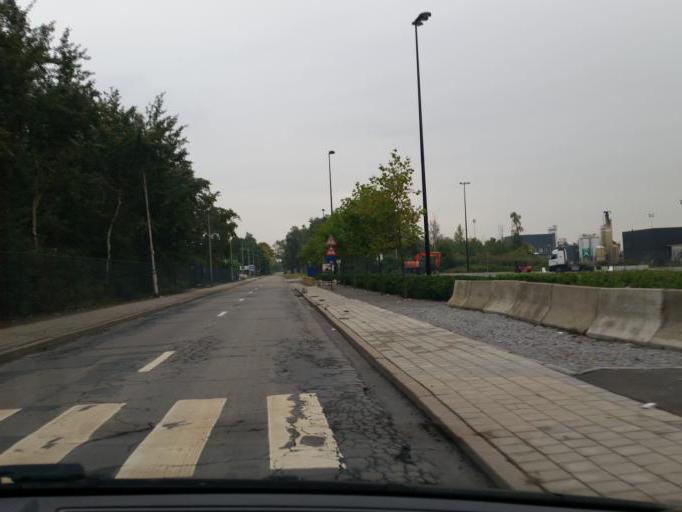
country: BE
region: Flanders
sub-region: Provincie Antwerpen
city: Hemiksem
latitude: 51.1622
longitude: 4.3375
